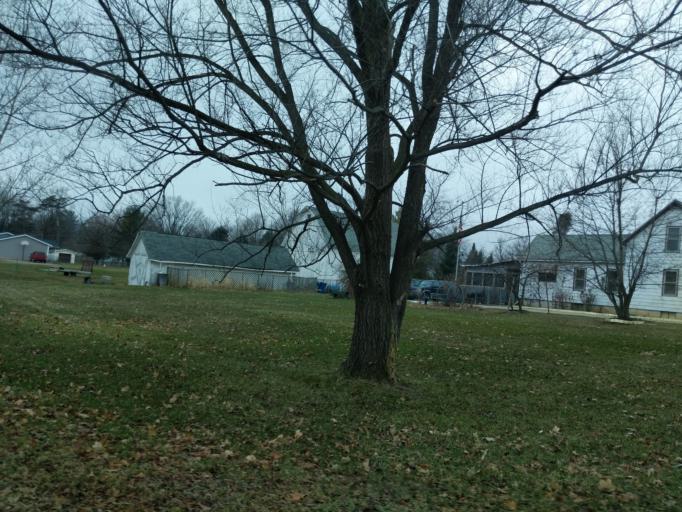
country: US
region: Michigan
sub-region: Lapeer County
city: Barnes Lake-Millers Lake
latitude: 43.3323
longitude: -83.3465
